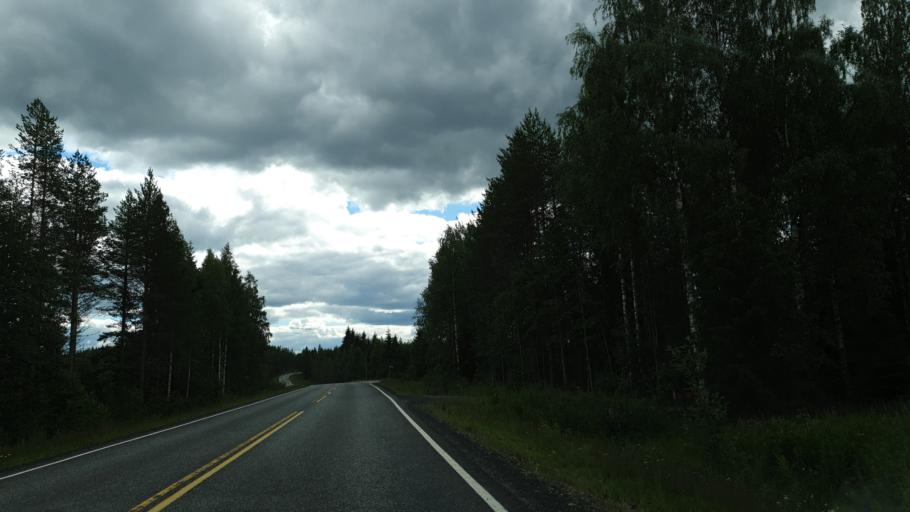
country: FI
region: Kainuu
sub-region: Kehys-Kainuu
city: Kuhmo
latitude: 63.9952
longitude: 29.6365
